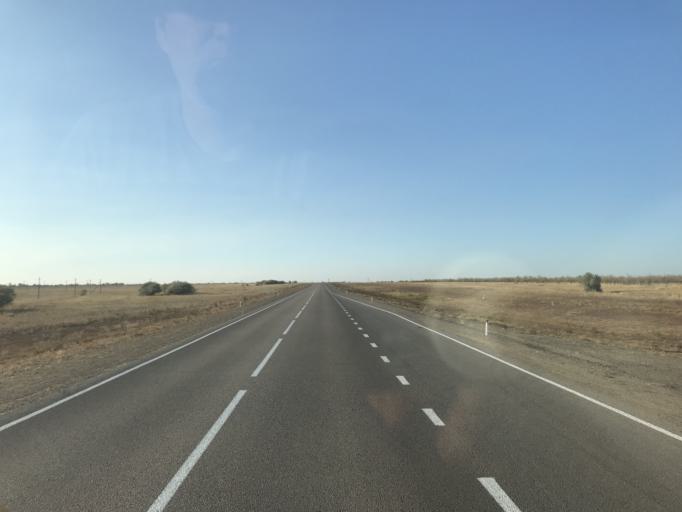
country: KZ
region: Pavlodar
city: Koktobe
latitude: 51.8839
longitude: 77.4162
